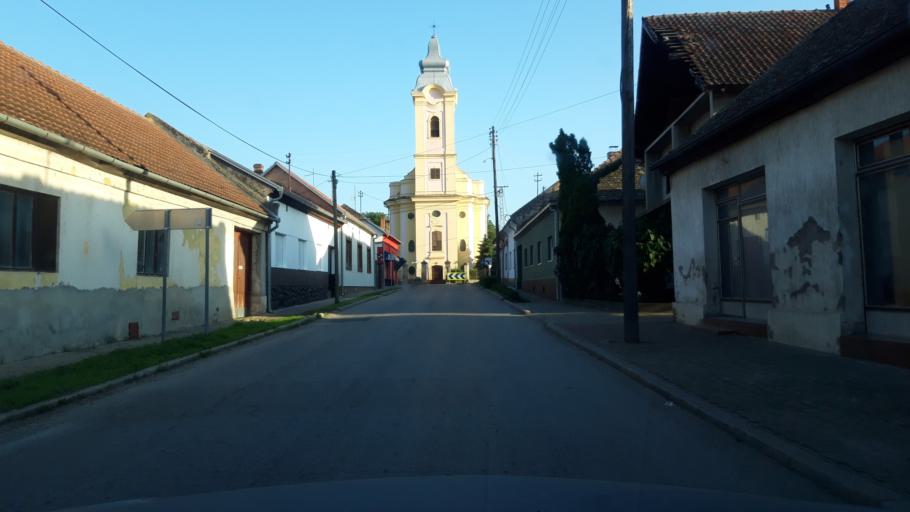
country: RS
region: Autonomna Pokrajina Vojvodina
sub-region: Juznobacki Okrug
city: Beocin
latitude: 45.2197
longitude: 19.6651
